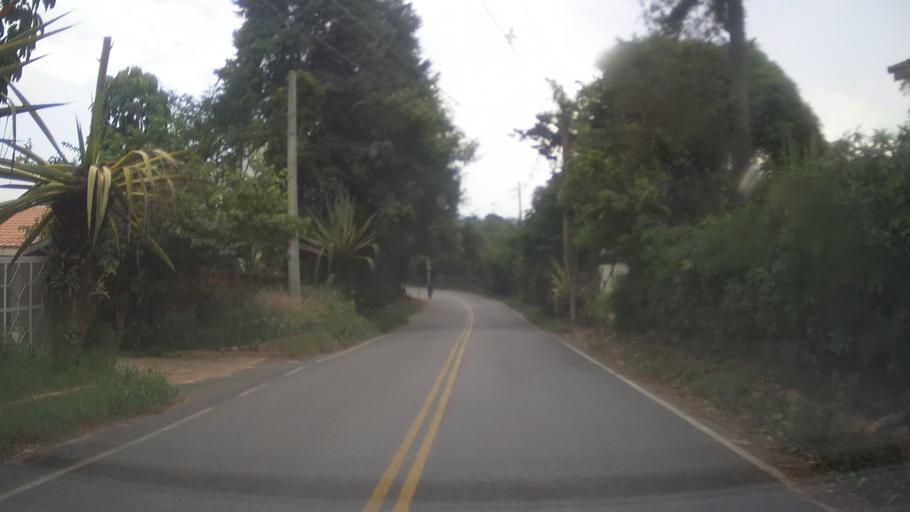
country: BR
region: Sao Paulo
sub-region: Itupeva
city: Itupeva
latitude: -23.1759
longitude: -47.1114
